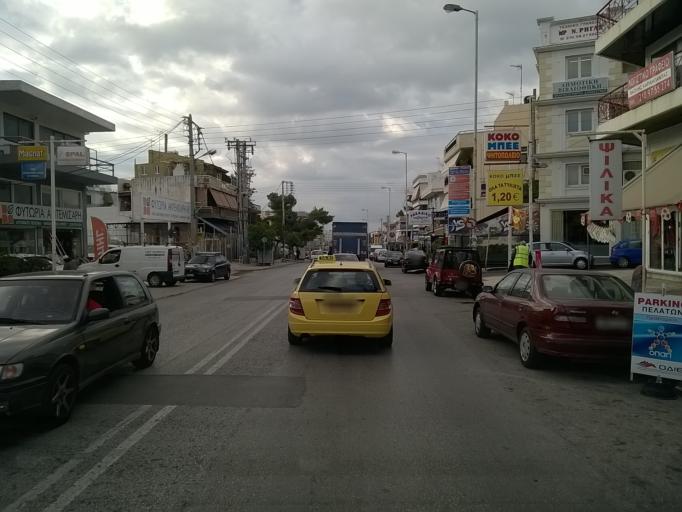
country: GR
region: Attica
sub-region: Nomarchia Athinas
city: Agios Dimitrios
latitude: 37.9317
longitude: 23.7274
